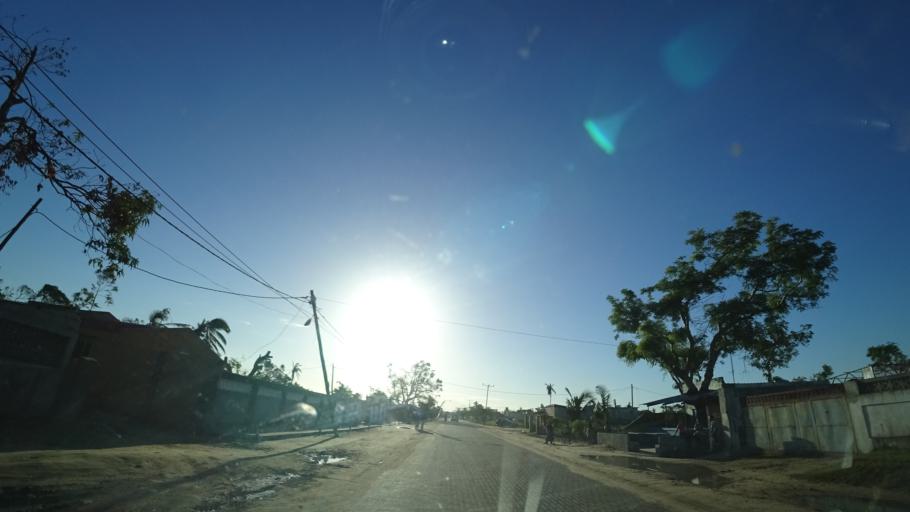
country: MZ
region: Sofala
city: Beira
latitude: -19.7398
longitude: 34.8323
